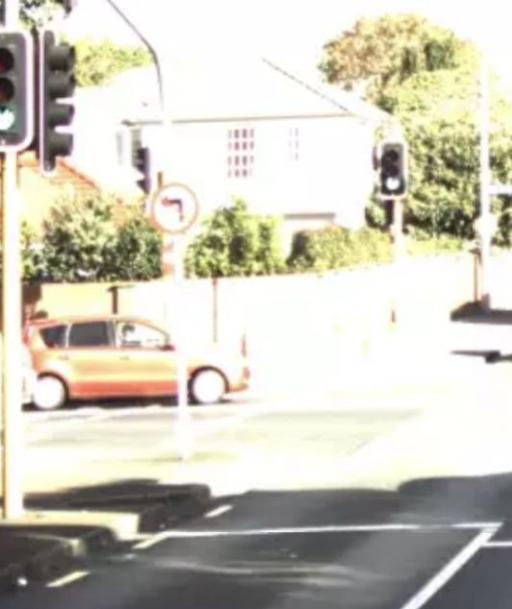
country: NZ
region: Auckland
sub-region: Auckland
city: Auckland
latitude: -36.8748
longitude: 174.7736
